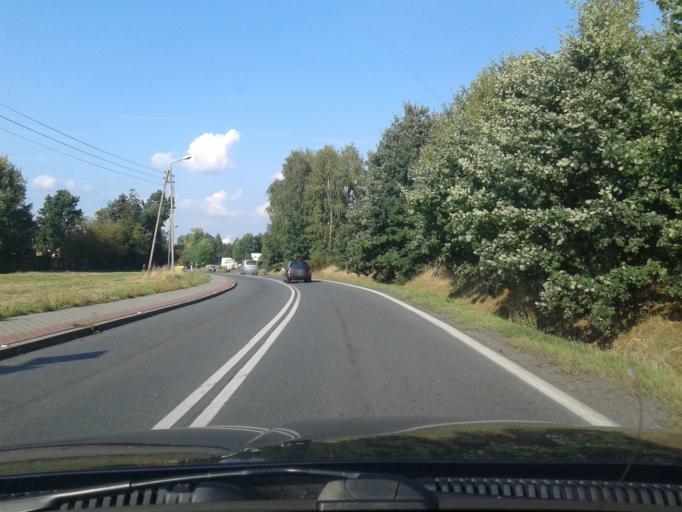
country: PL
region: Silesian Voivodeship
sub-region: Powiat wodzislawski
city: Turza Slaska
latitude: 49.9808
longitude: 18.4516
